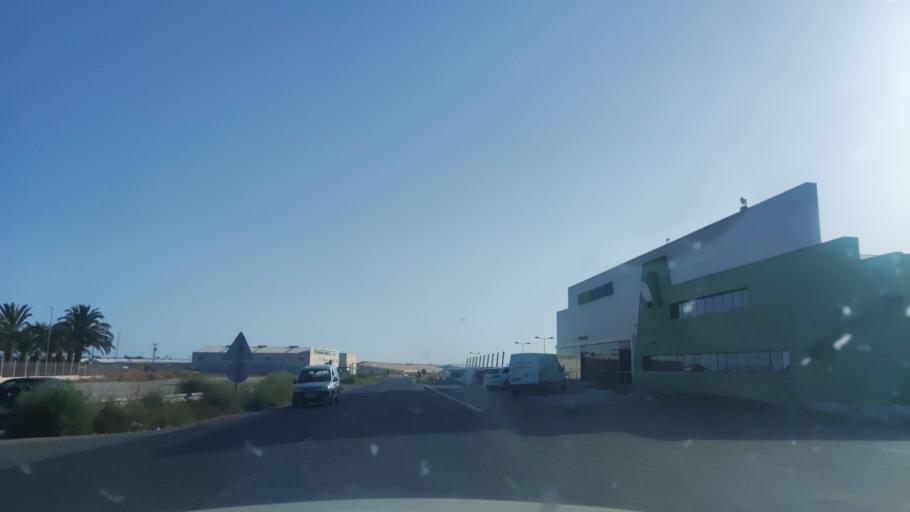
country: ES
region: Murcia
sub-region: Murcia
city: San Javier
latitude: 37.7887
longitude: -0.8743
